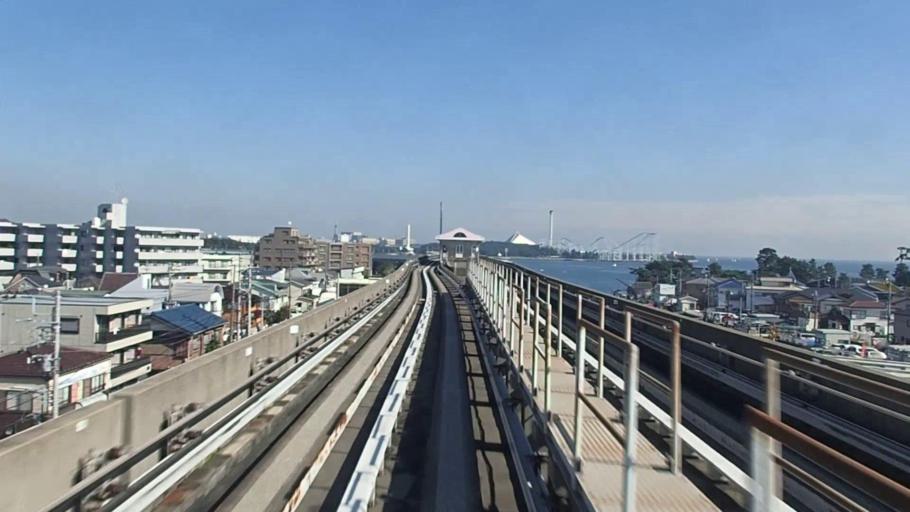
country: JP
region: Kanagawa
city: Yokosuka
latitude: 35.3300
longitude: 139.6304
